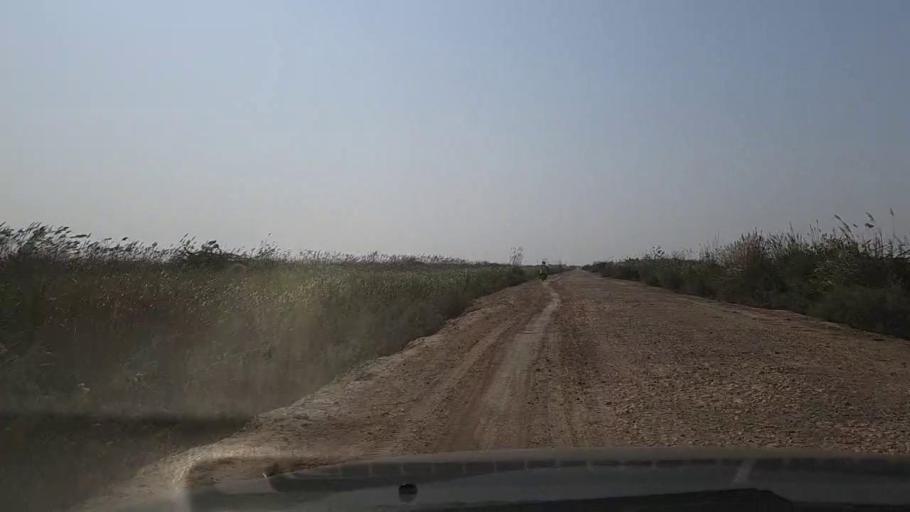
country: PK
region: Sindh
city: Mirpur Sakro
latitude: 24.3730
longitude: 67.6528
